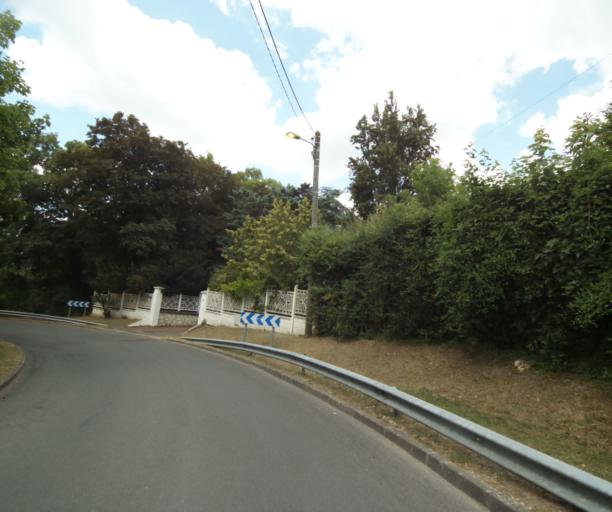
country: FR
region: Ile-de-France
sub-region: Departement de Seine-et-Marne
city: Hericy
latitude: 48.4501
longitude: 2.7684
